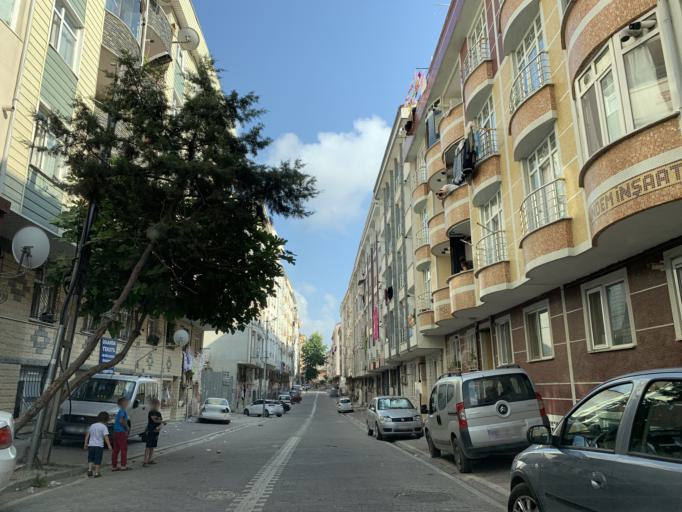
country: TR
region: Istanbul
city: Esenyurt
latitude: 41.0321
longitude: 28.6759
